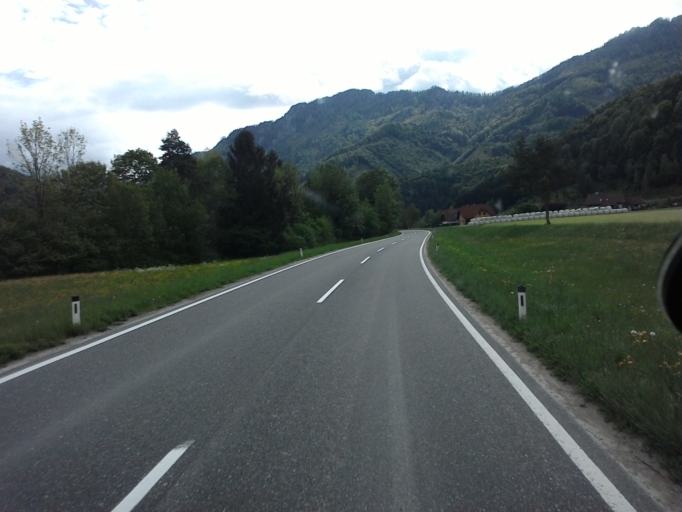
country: AT
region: Upper Austria
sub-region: Politischer Bezirk Kirchdorf an der Krems
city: Micheldorf in Oberoesterreich
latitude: 47.8405
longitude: 14.1640
